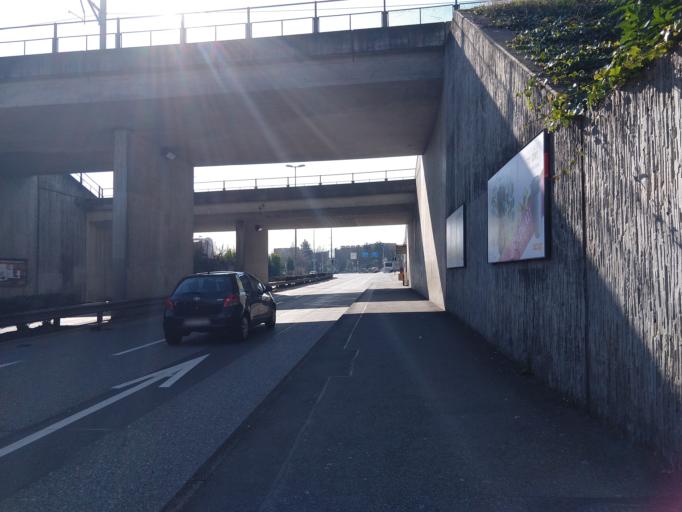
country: CH
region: Geneva
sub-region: Geneva
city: Vernier
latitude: 46.2203
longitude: 6.0963
